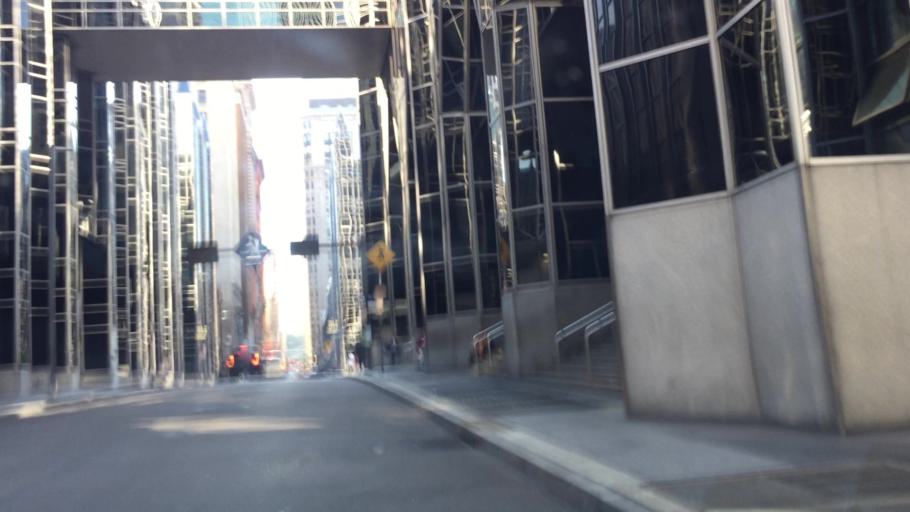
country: US
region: Pennsylvania
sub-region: Allegheny County
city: Pittsburgh
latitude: 40.4403
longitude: -80.0040
